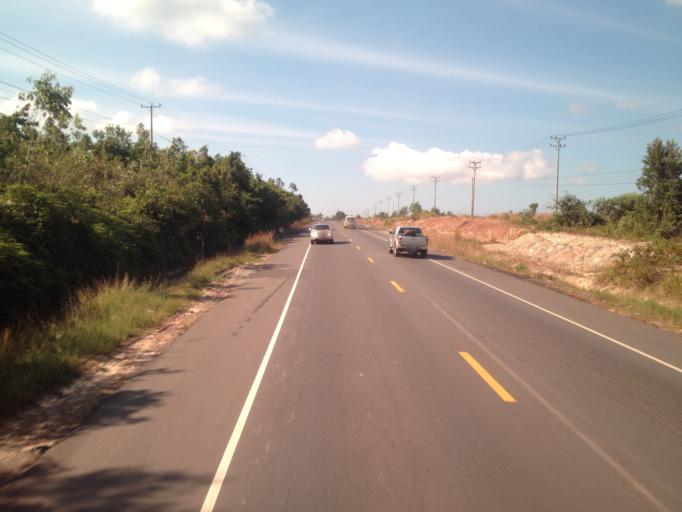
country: KH
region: Preah Sihanouk
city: Sihanoukville
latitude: 10.6038
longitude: 103.6107
